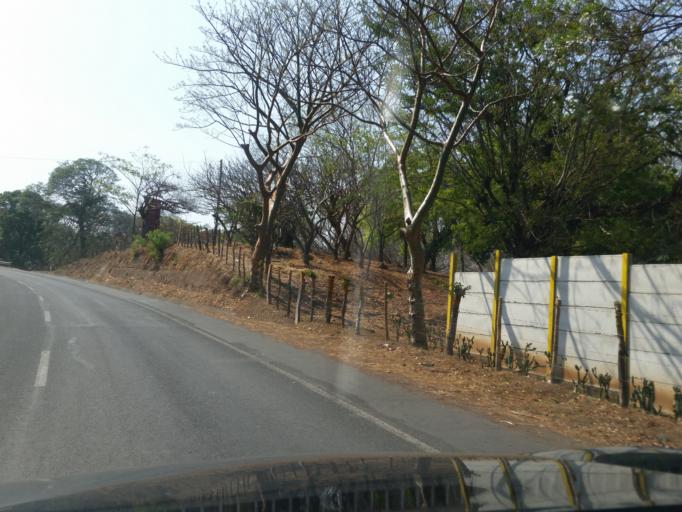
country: NI
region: Granada
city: Granada
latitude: 11.9613
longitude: -85.9942
